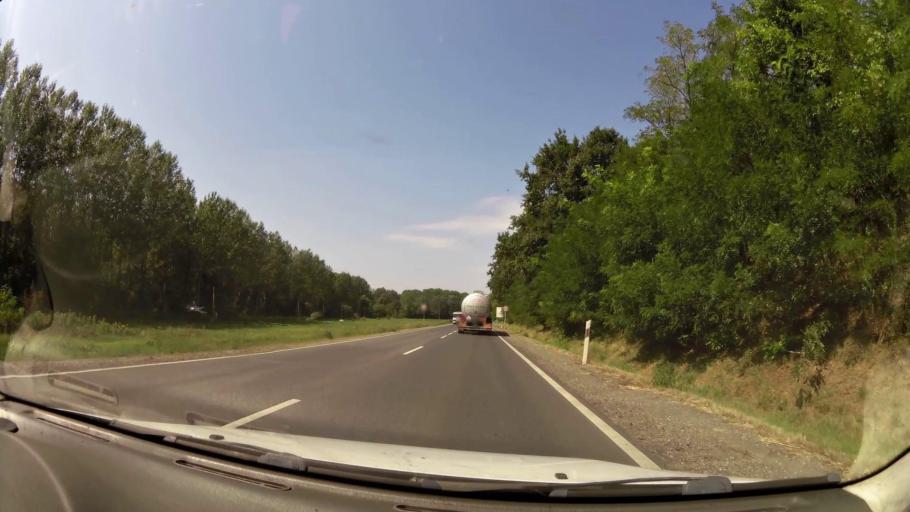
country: HU
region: Pest
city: Gyomro
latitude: 47.4282
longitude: 19.4268
